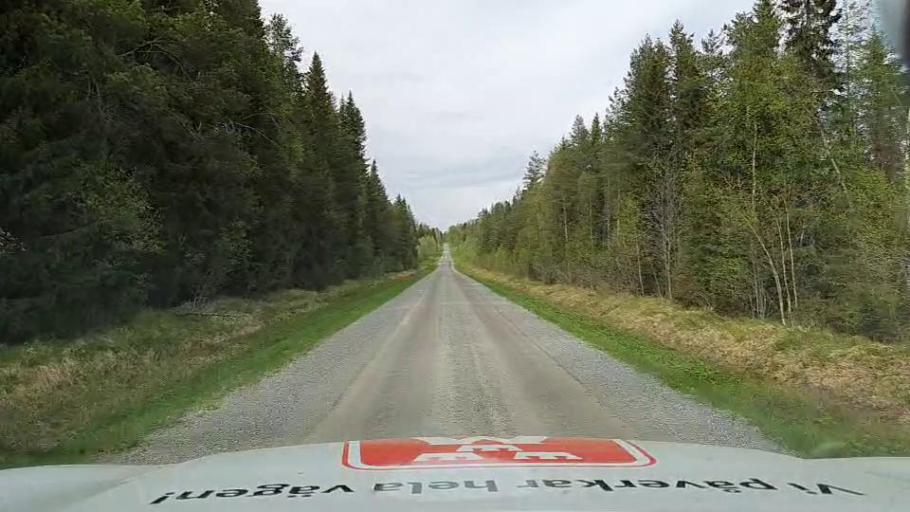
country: SE
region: Jaemtland
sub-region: OEstersunds Kommun
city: Brunflo
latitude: 62.6075
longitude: 14.9404
